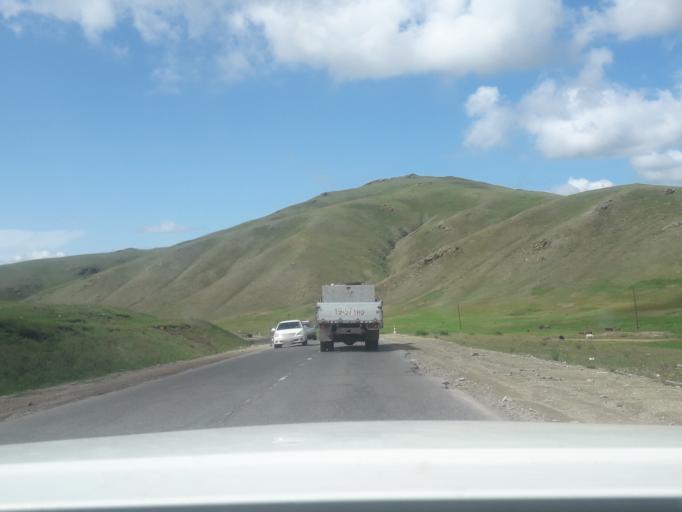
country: MN
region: Central Aimak
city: Ihsueuej
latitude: 48.1875
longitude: 106.3698
